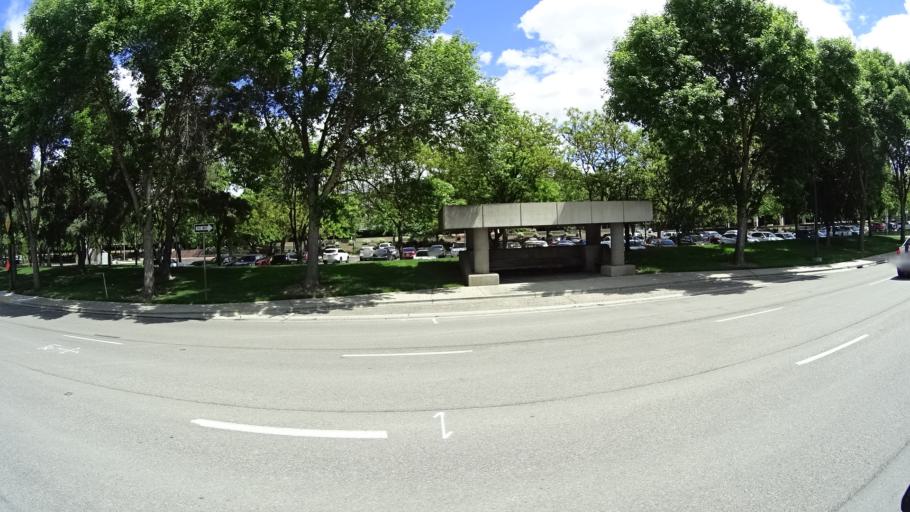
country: US
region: Idaho
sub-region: Ada County
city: Boise
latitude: 43.6042
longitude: -116.1910
